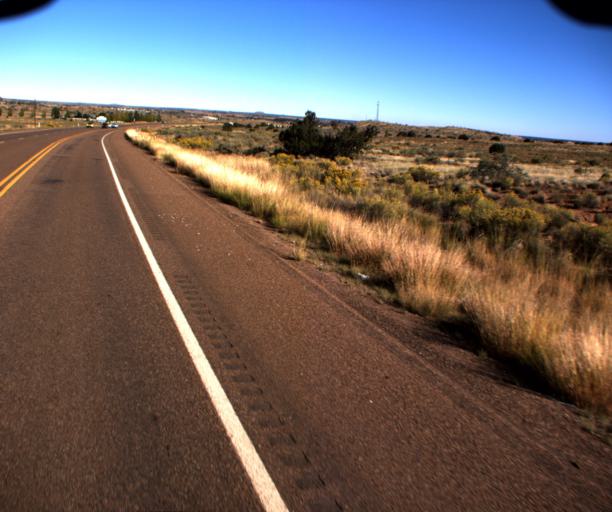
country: US
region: Arizona
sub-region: Navajo County
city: Taylor
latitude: 34.4332
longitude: -110.0938
